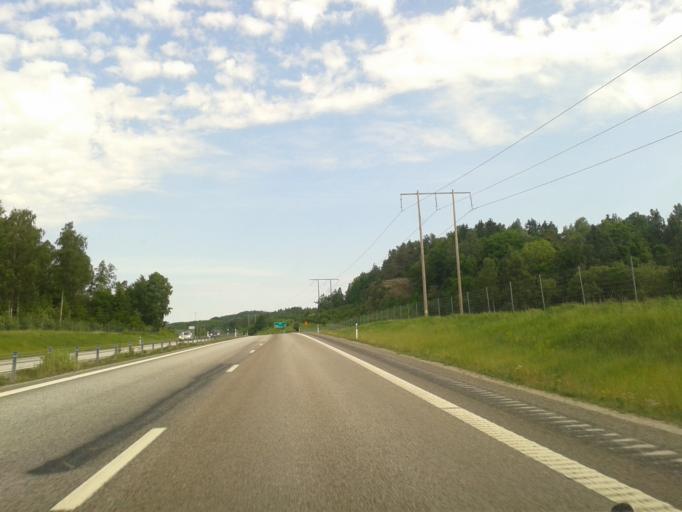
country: SE
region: Vaestra Goetaland
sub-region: Munkedals Kommun
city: Munkedal
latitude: 58.5241
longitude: 11.5463
